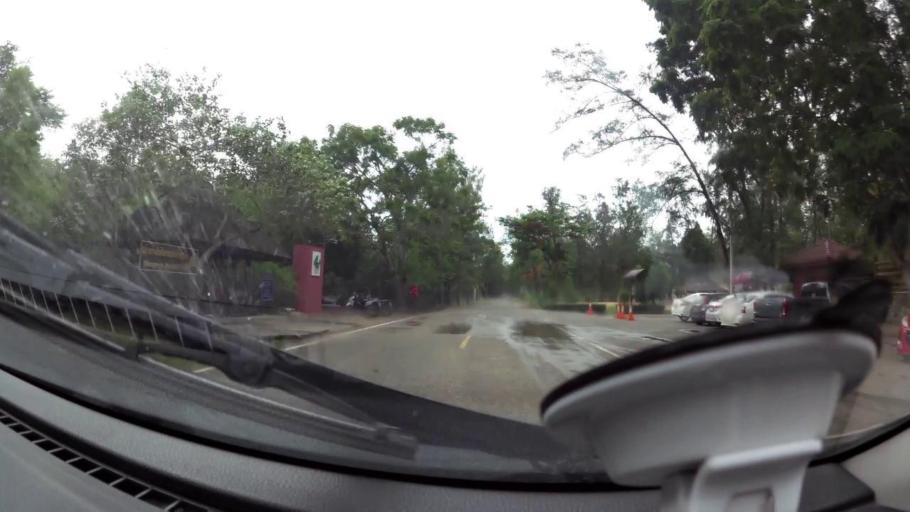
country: TH
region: Prachuap Khiri Khan
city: Pran Buri
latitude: 12.4135
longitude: 99.9852
